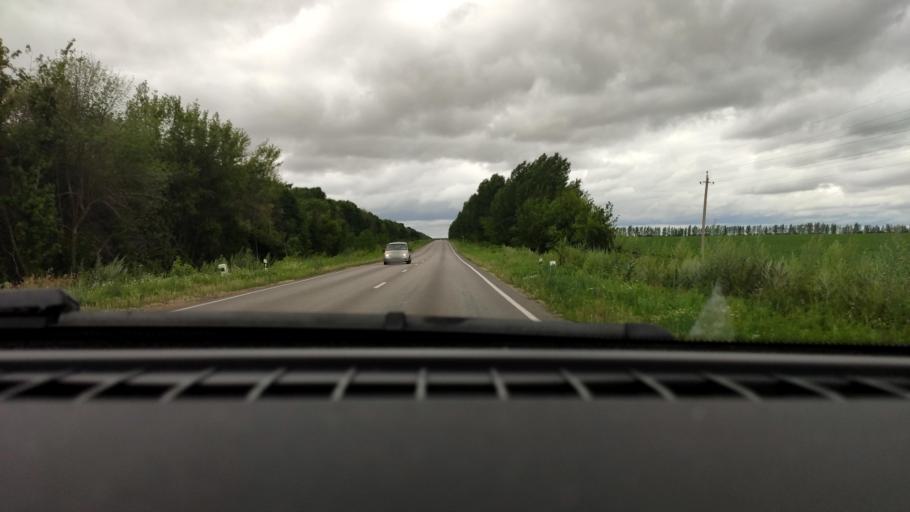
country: RU
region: Voronezj
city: Latnaya
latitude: 51.7740
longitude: 38.8986
